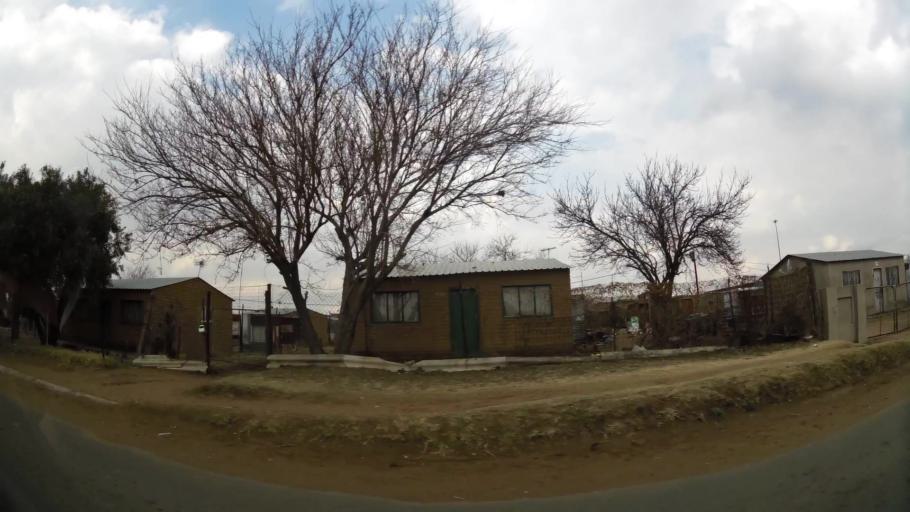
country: ZA
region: Orange Free State
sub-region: Fezile Dabi District Municipality
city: Sasolburg
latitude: -26.8529
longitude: 27.8772
